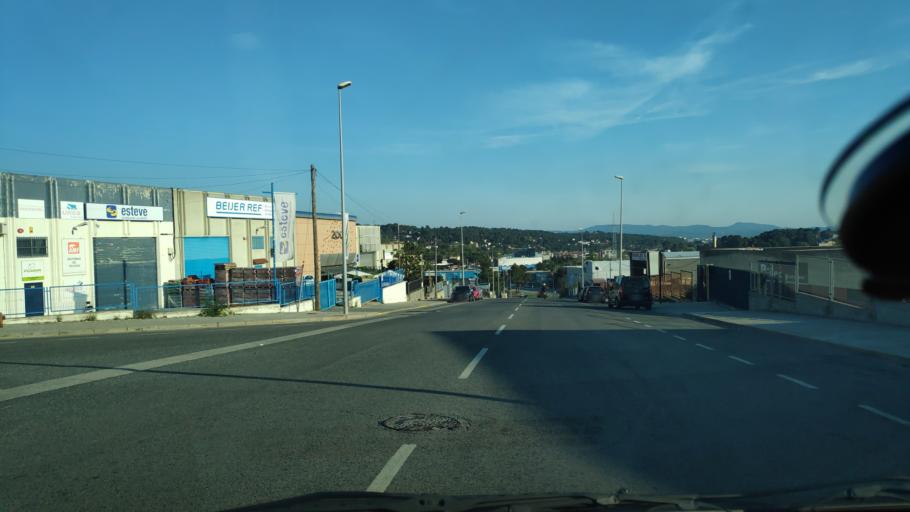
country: ES
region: Catalonia
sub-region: Provincia de Barcelona
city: Terrassa
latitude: 41.5383
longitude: 2.0314
